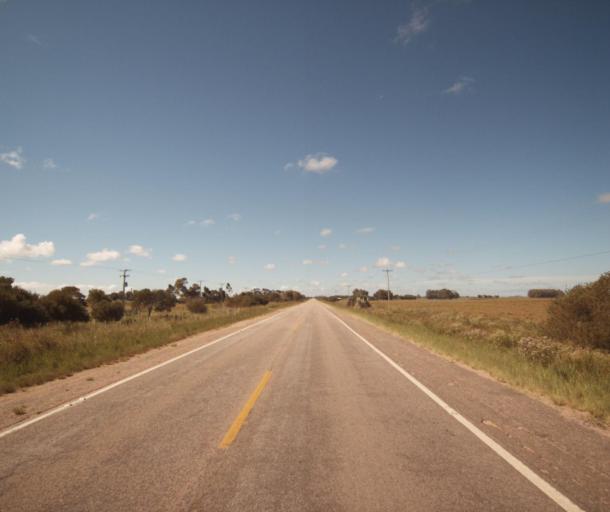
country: BR
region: Rio Grande do Sul
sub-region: Chui
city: Chui
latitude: -33.6410
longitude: -53.4220
